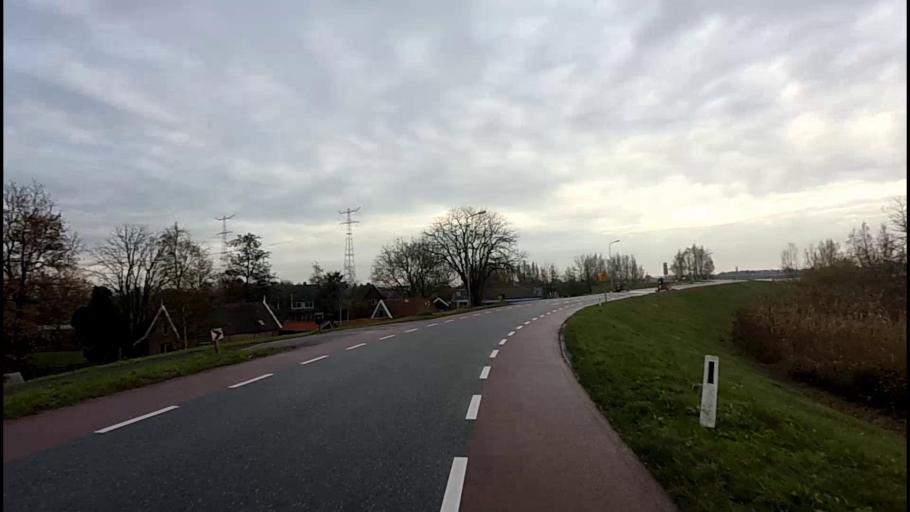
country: NL
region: South Holland
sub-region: Gemeente Alblasserdam
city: Alblasserdam
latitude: 51.8931
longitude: 4.6583
